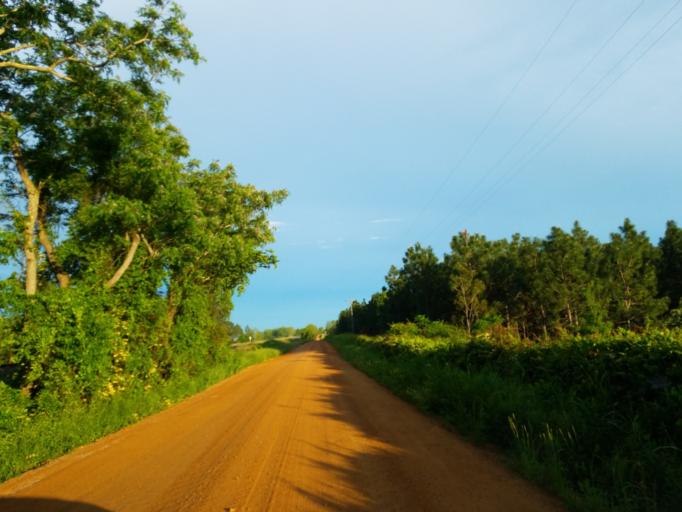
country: US
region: Georgia
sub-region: Turner County
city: Ashburn
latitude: 31.6133
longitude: -83.6028
